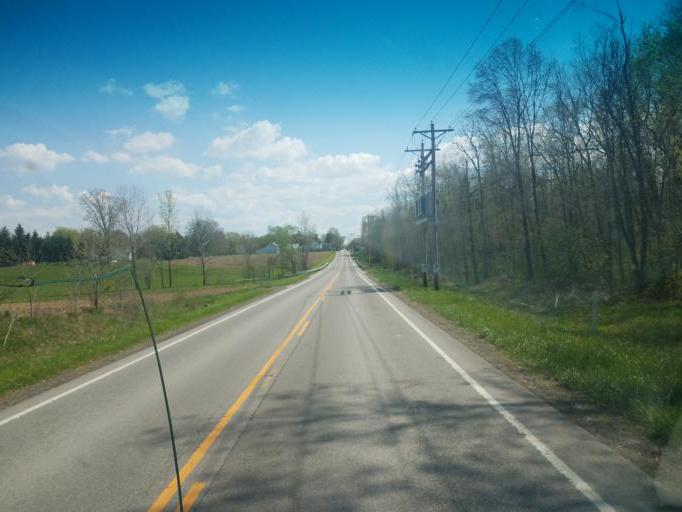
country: US
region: Ohio
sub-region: Wayne County
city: West Salem
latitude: 40.9209
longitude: -82.1090
